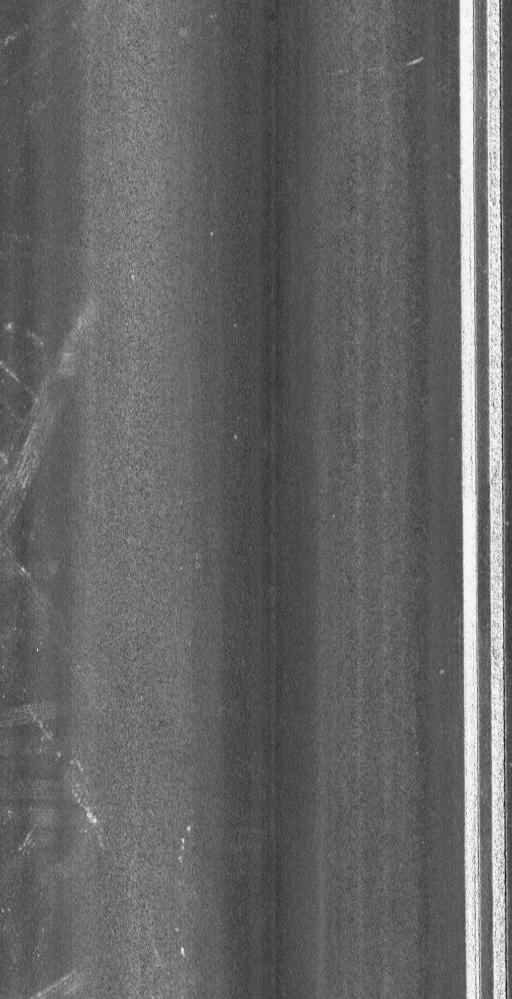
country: US
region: Vermont
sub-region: Chittenden County
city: Burlington
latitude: 44.3713
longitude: -73.2249
